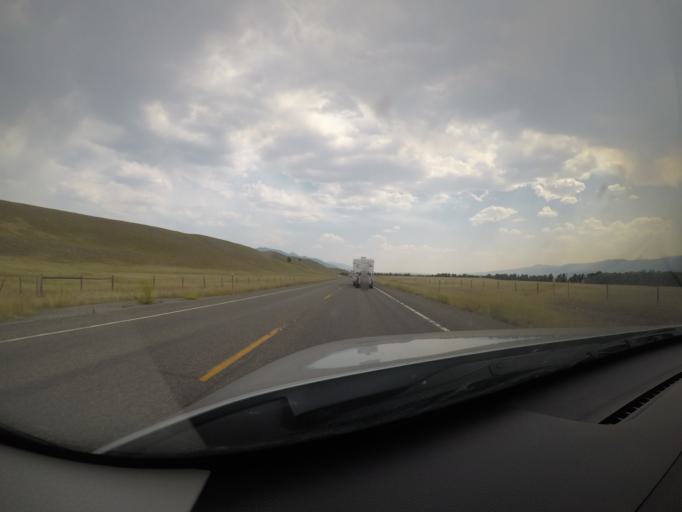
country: US
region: Montana
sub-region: Gallatin County
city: Big Sky
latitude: 45.1087
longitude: -111.6542
